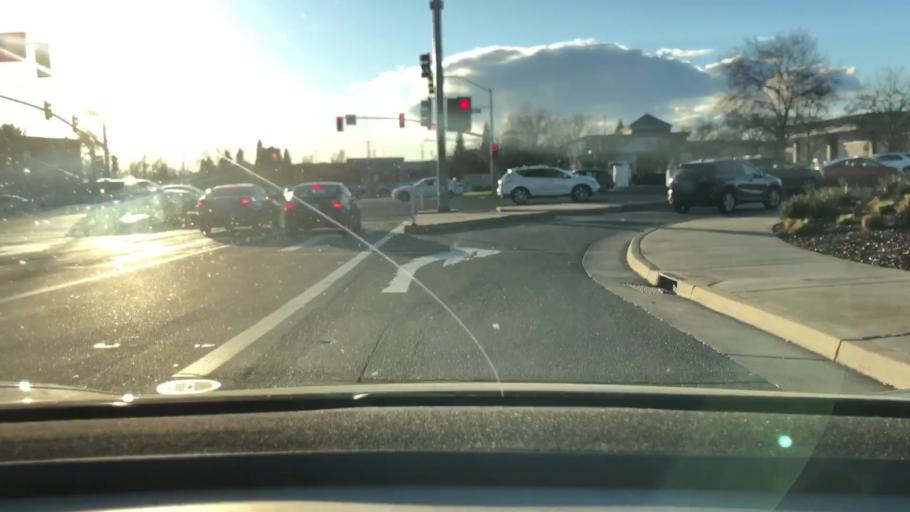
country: US
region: California
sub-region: Placer County
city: Roseville
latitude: 38.7722
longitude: -121.2652
